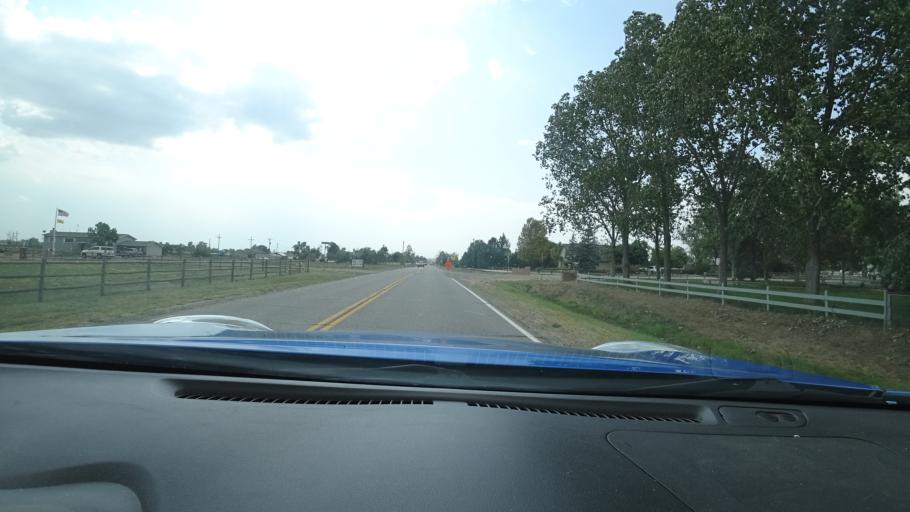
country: US
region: Colorado
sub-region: Adams County
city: Todd Creek
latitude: 39.9217
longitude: -104.8403
